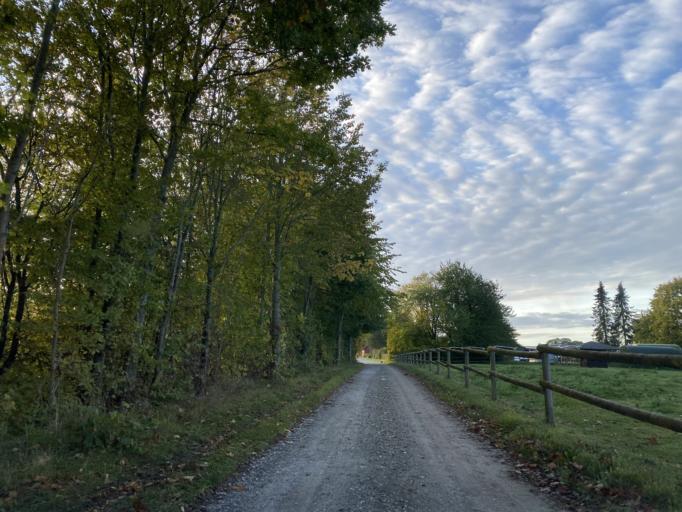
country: DK
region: Capital Region
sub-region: Allerod Kommune
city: Lynge
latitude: 55.8178
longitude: 12.2834
